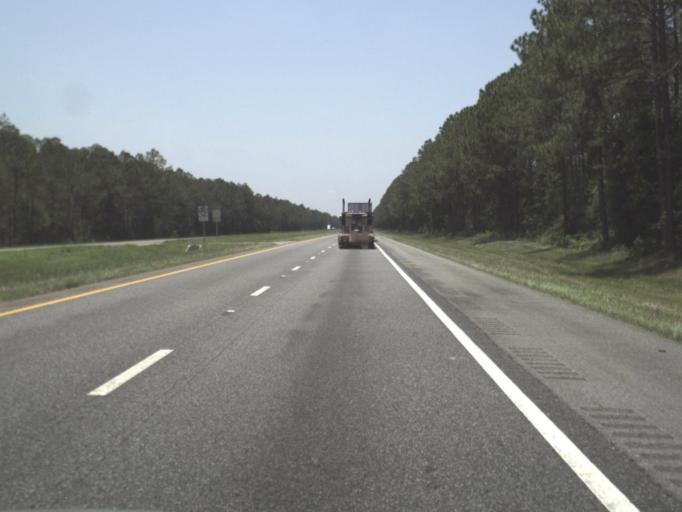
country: US
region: Florida
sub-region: Union County
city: Lake Butler
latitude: 30.2544
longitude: -82.3548
